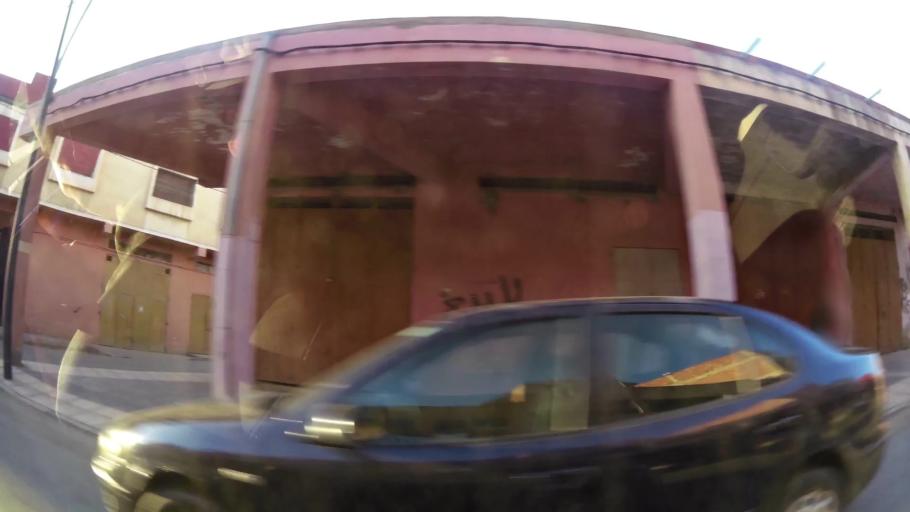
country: MA
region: Oriental
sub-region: Berkane-Taourirt
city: Berkane
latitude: 34.9222
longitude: -2.3341
